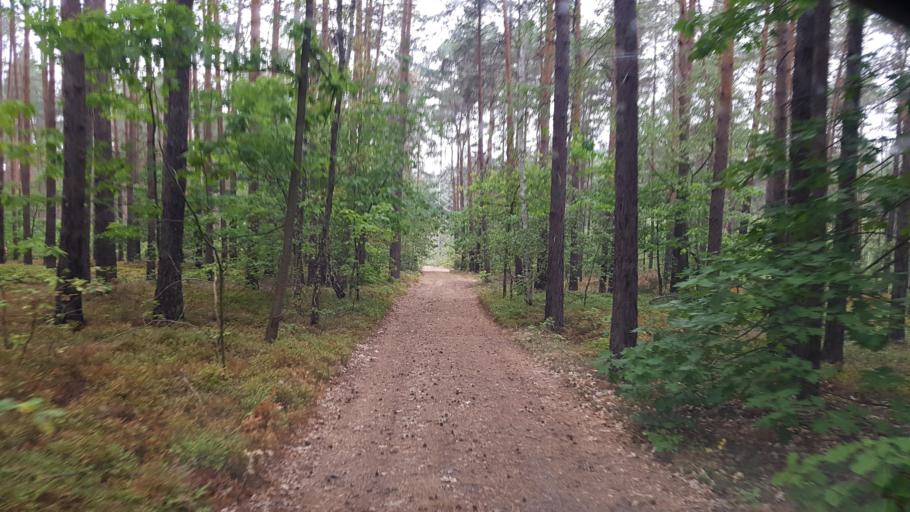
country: DE
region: Brandenburg
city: Sallgast
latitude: 51.6021
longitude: 13.8338
